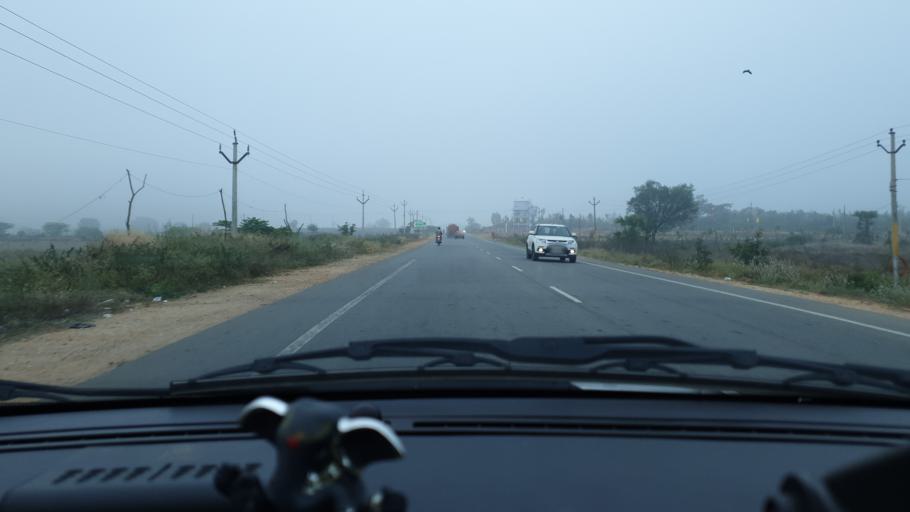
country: IN
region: Telangana
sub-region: Mahbubnagar
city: Farrukhnagar
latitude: 16.9186
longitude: 78.5272
